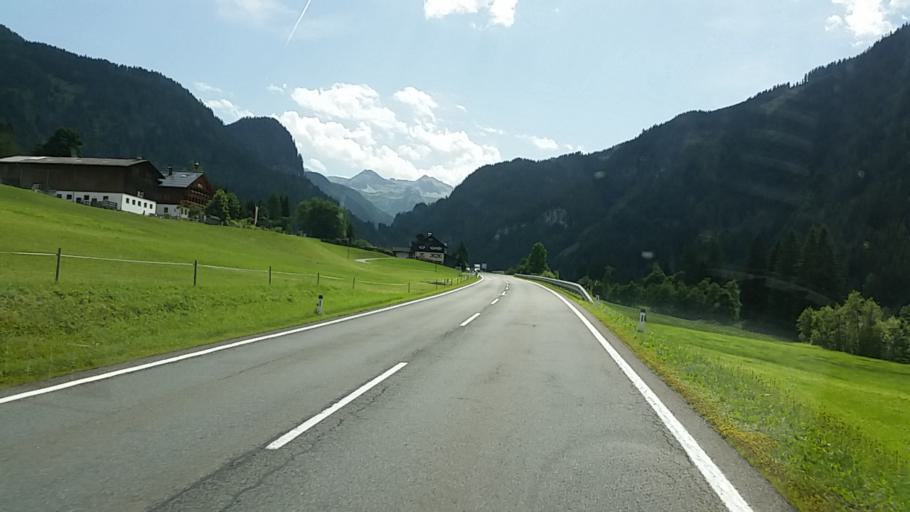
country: AT
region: Salzburg
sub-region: Politischer Bezirk Sankt Johann im Pongau
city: Untertauern
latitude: 47.3124
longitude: 13.5080
